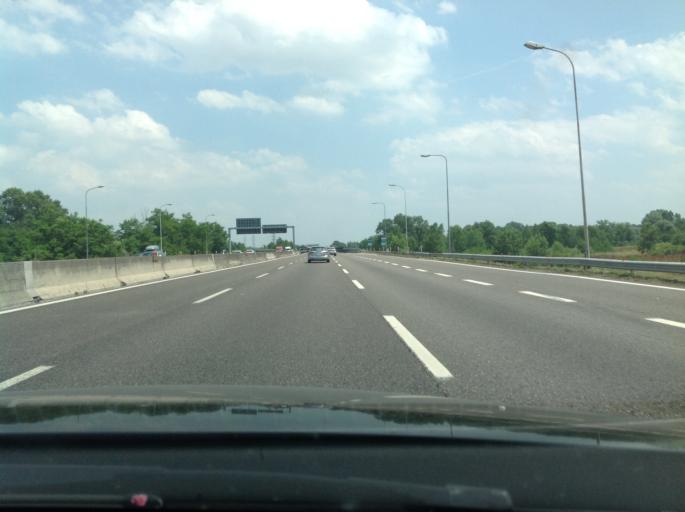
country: IT
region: Emilia-Romagna
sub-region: Provincia di Parma
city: Ponte Taro
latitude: 44.8641
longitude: 10.2376
